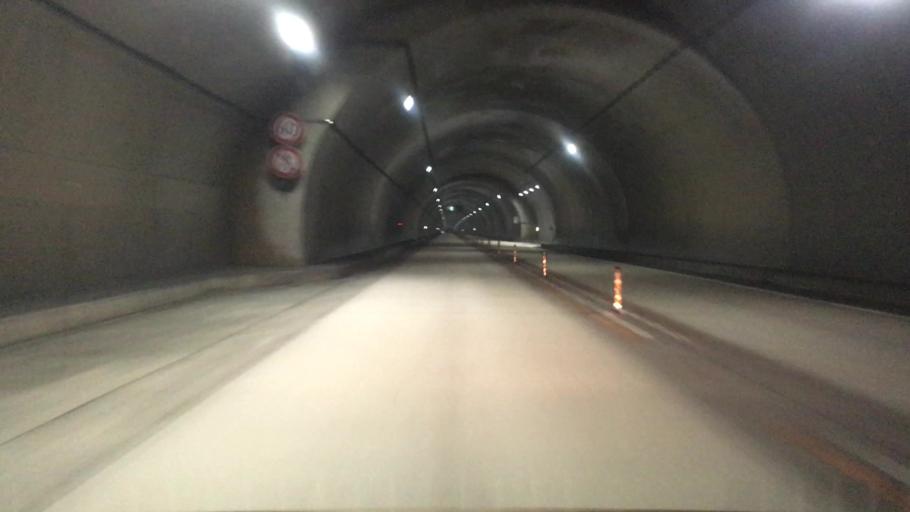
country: JP
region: Tottori
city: Tottori
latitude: 35.6083
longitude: 134.3855
